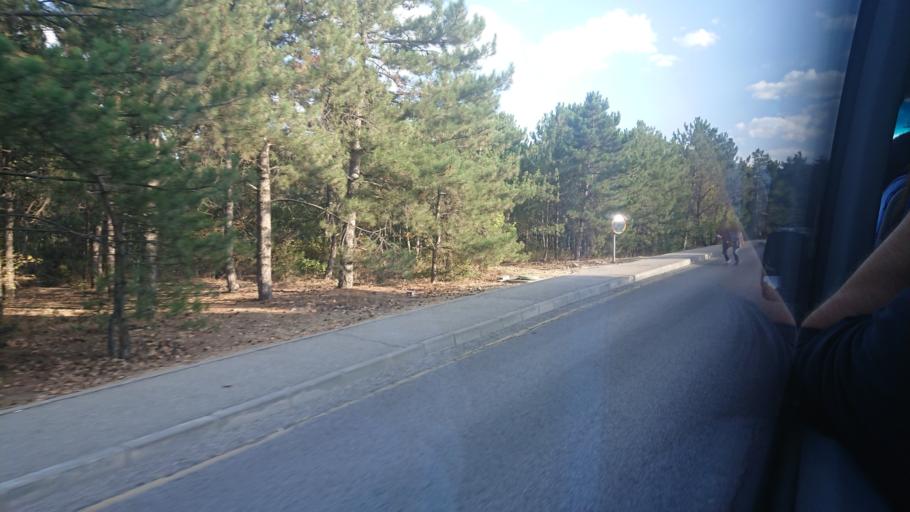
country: TR
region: Ankara
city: Ankara
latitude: 39.8908
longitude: 32.7842
